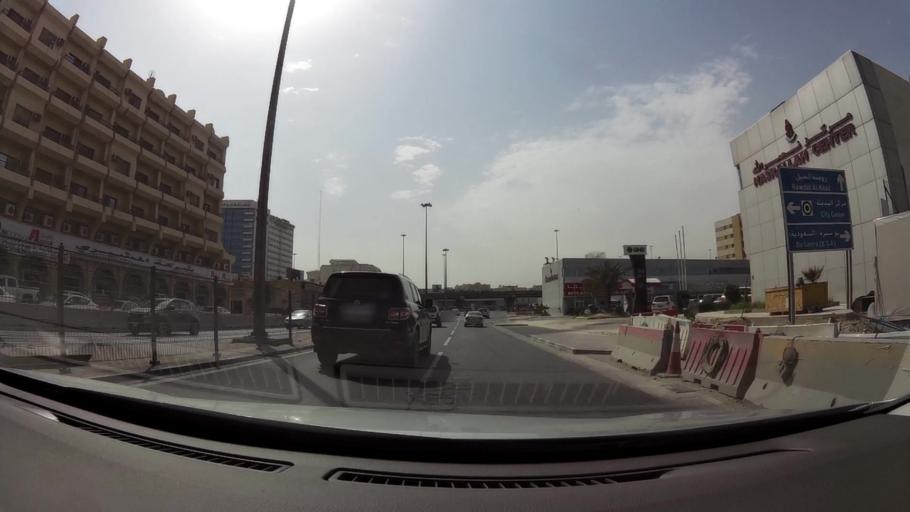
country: QA
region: Baladiyat ad Dawhah
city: Doha
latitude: 25.2807
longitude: 51.5184
